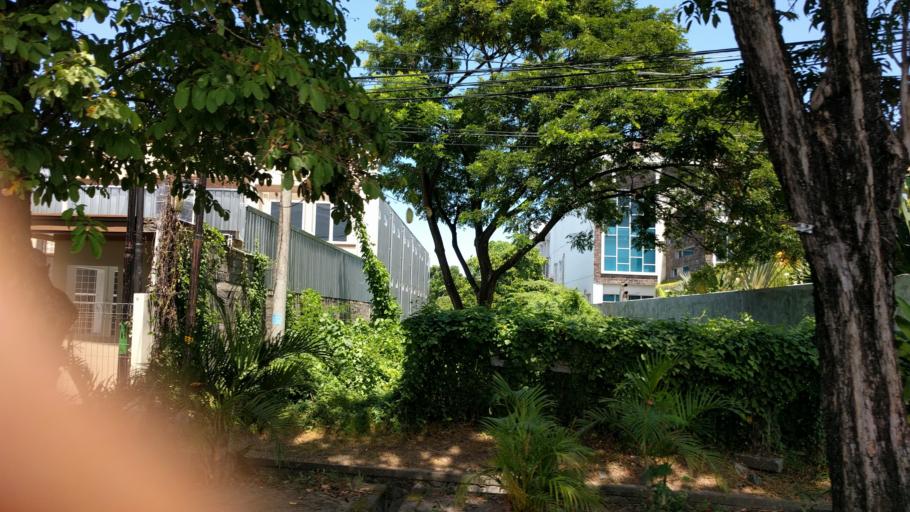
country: ID
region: Bali
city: Kuta
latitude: -8.7040
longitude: 115.1846
